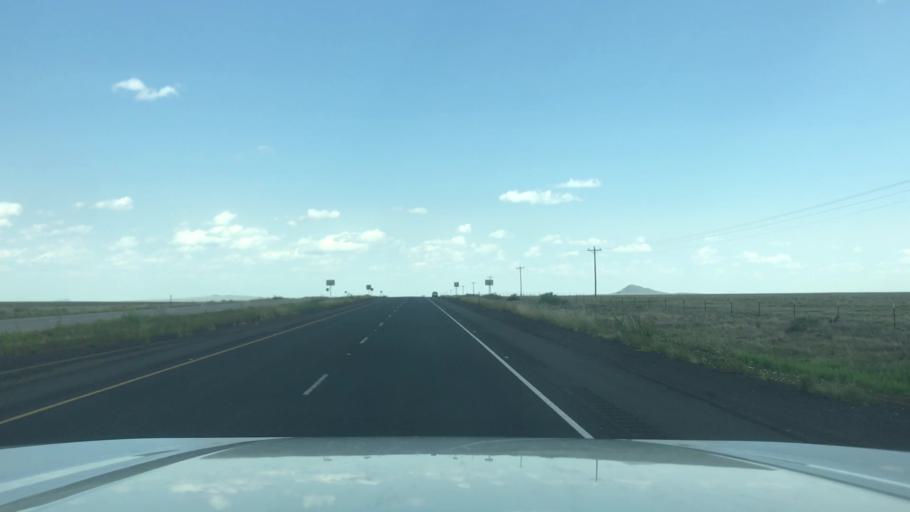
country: US
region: New Mexico
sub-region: Union County
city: Clayton
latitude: 36.6337
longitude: -103.7182
